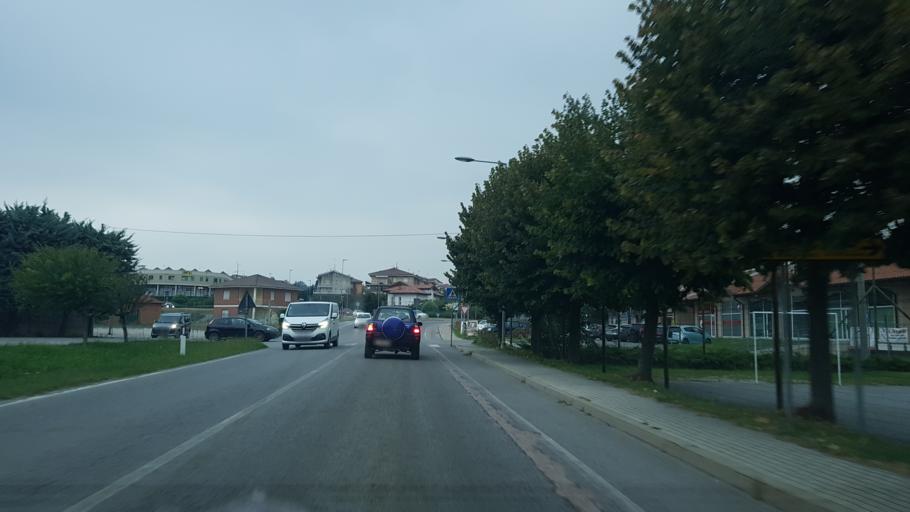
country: IT
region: Piedmont
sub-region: Provincia di Cuneo
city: Villanova Mondovi
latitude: 44.3474
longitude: 7.7731
